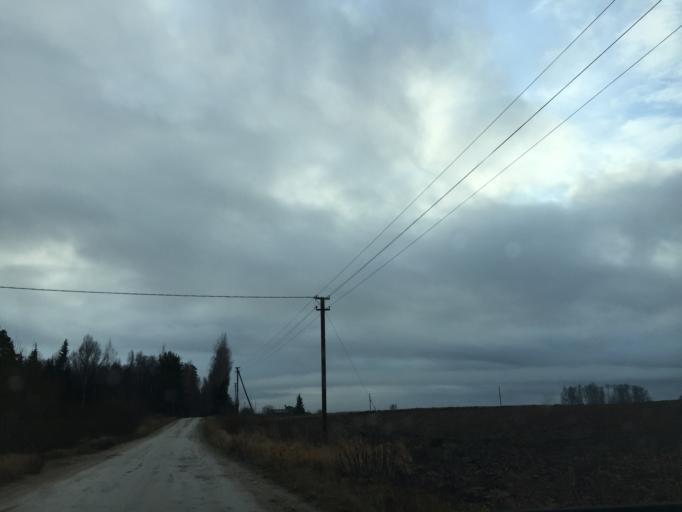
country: LV
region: Vainode
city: Vainode
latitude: 56.6081
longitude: 21.7985
